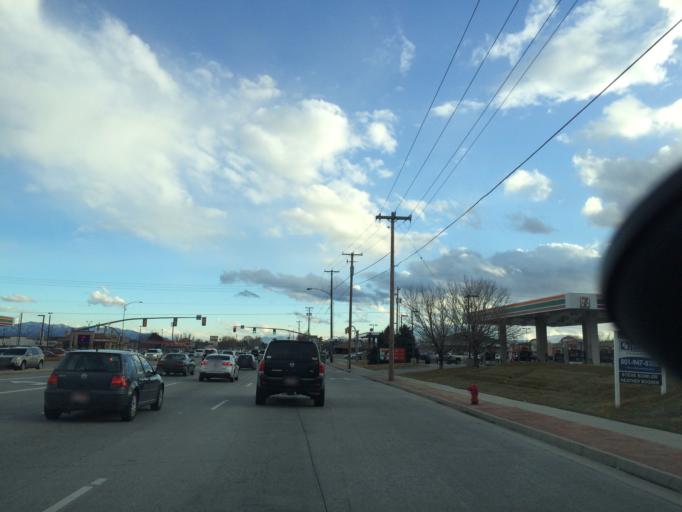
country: US
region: Utah
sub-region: Salt Lake County
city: West Jordan
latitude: 40.6252
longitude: -111.9389
